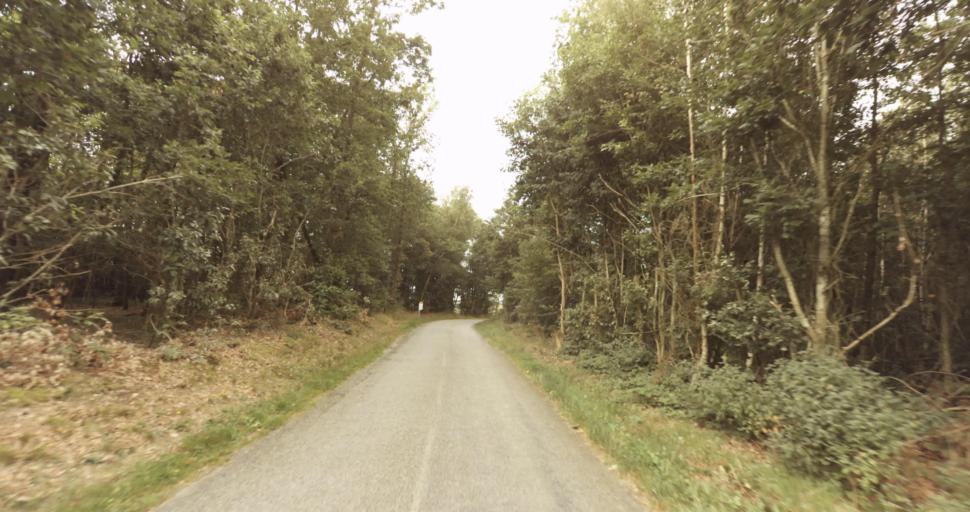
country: FR
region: Centre
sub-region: Departement d'Eure-et-Loir
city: Vert-en-Drouais
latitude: 48.7791
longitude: 1.3135
